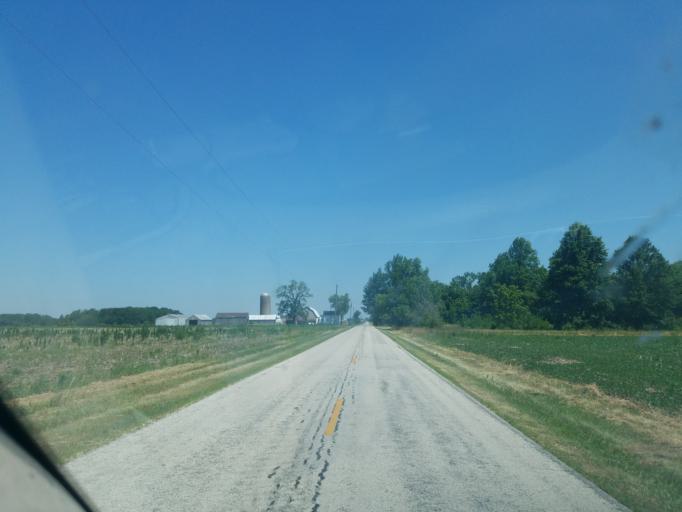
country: US
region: Ohio
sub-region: Mercer County
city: Coldwater
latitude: 40.5695
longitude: -84.7082
